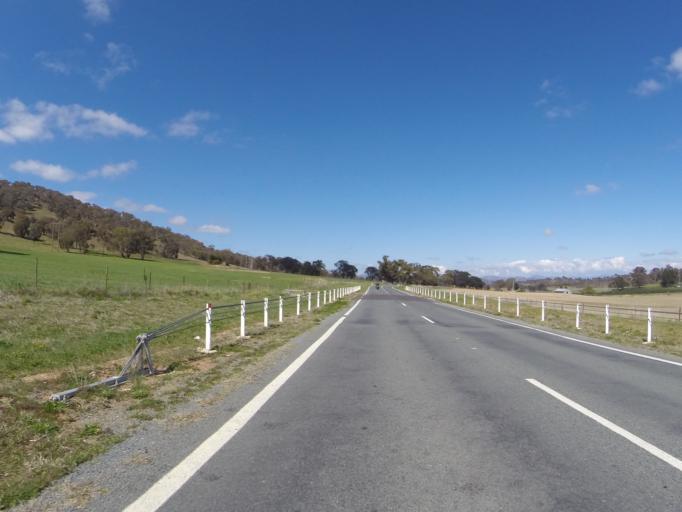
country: AU
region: New South Wales
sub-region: Queanbeyan
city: Queanbeyan
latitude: -35.3059
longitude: 149.2509
